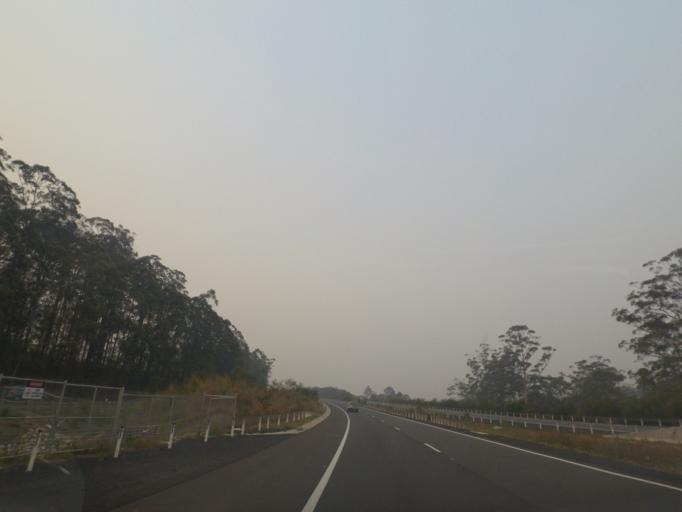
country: AU
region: New South Wales
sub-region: Nambucca Shire
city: Macksville
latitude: -30.7411
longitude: 152.9199
